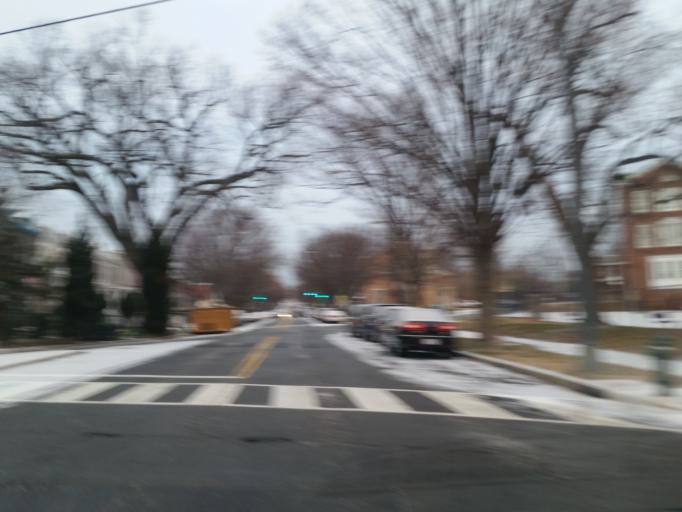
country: US
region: Maryland
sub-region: Montgomery County
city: Takoma Park
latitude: 38.9529
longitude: -77.0254
